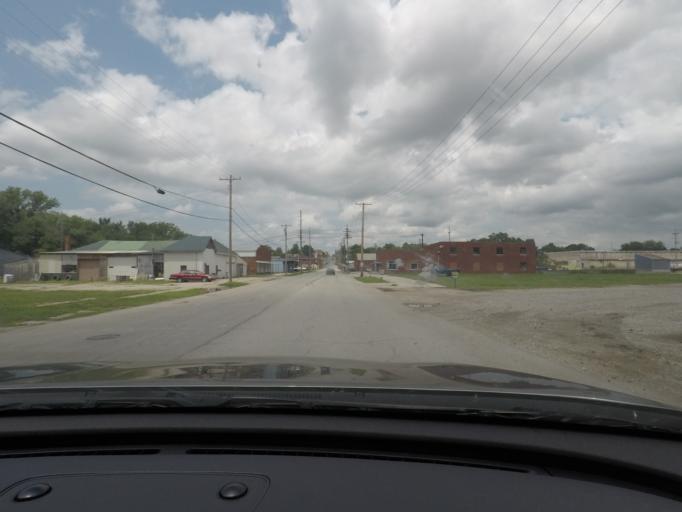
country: US
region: Missouri
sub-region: Carroll County
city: Carrollton
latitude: 39.3501
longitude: -93.4959
